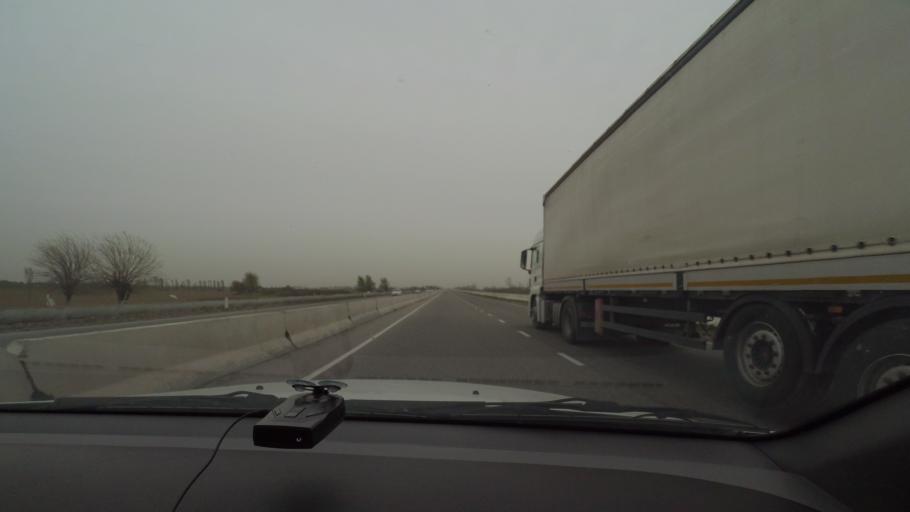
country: UZ
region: Jizzax
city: Gagarin
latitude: 40.4813
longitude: 68.2859
